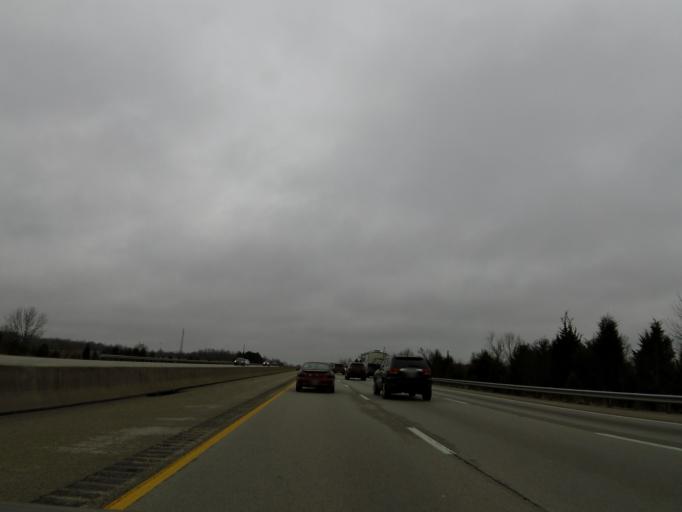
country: US
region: Kentucky
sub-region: Scott County
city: Georgetown
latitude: 38.3974
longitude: -84.5765
